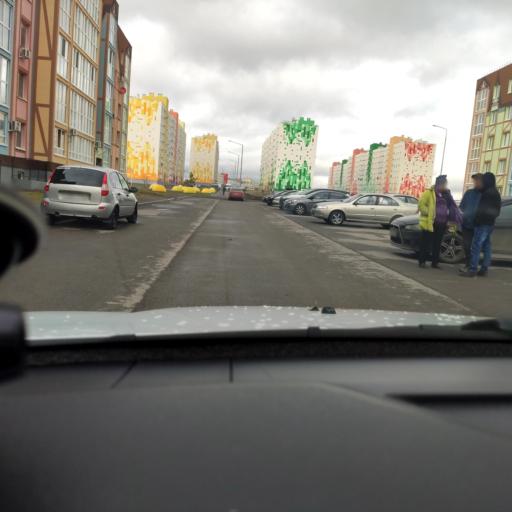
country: RU
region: Samara
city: Petra-Dubrava
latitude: 53.2992
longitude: 50.3270
